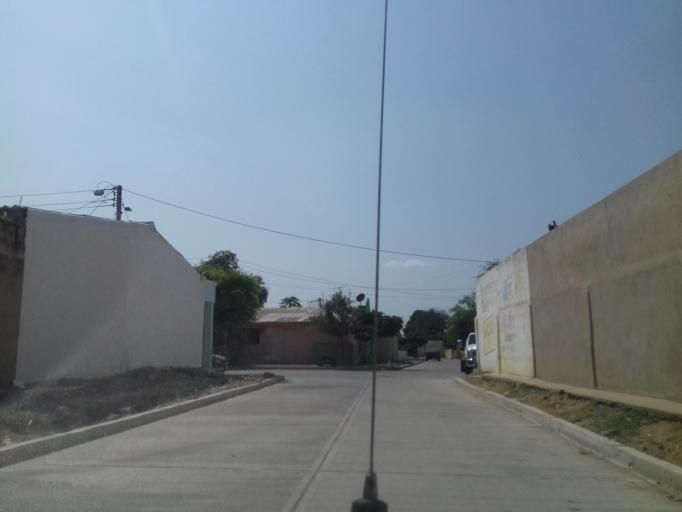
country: CO
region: La Guajira
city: Maicao
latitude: 11.3821
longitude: -72.2541
